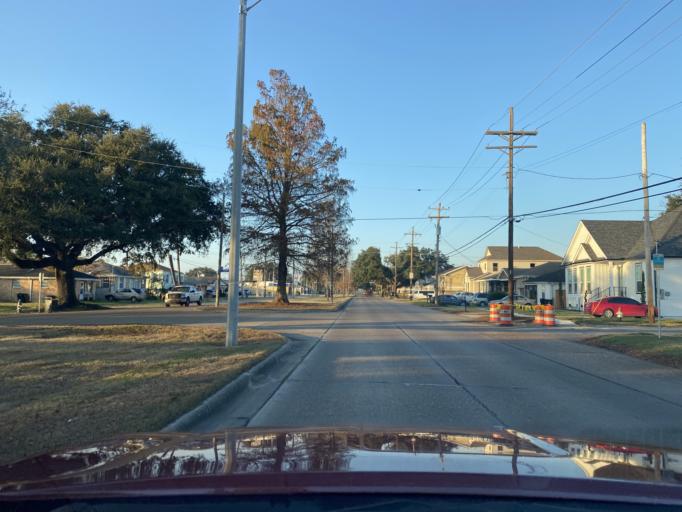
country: US
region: Louisiana
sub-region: Orleans Parish
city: New Orleans
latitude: 30.0202
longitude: -90.0516
